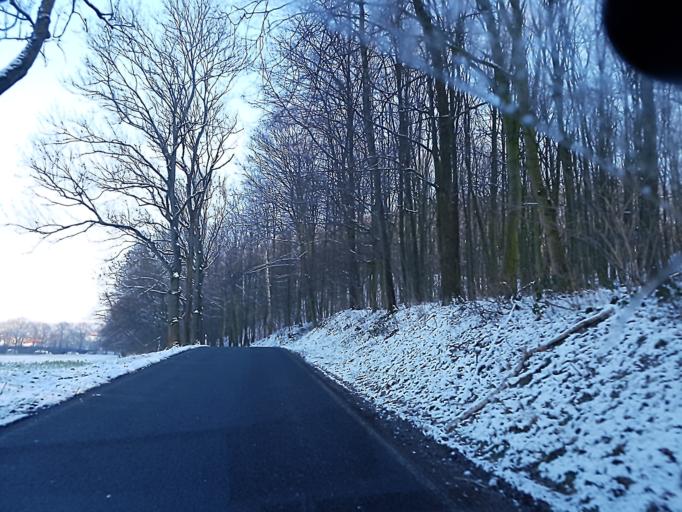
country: DE
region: Saxony
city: Leisnig
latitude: 51.1515
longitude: 12.9739
